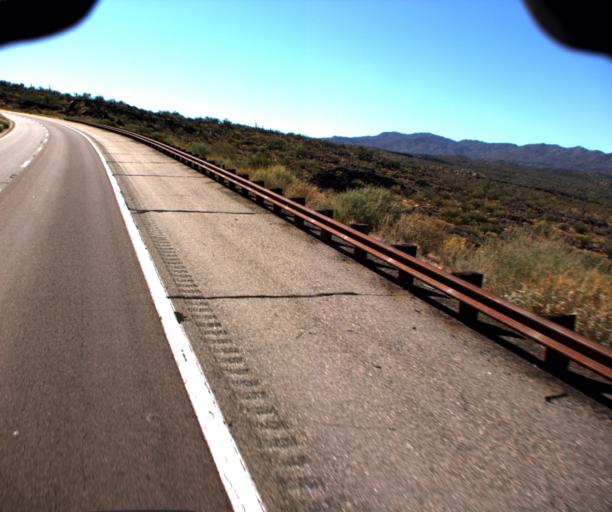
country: US
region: Arizona
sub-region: Yavapai County
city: Bagdad
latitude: 34.5032
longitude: -113.4082
